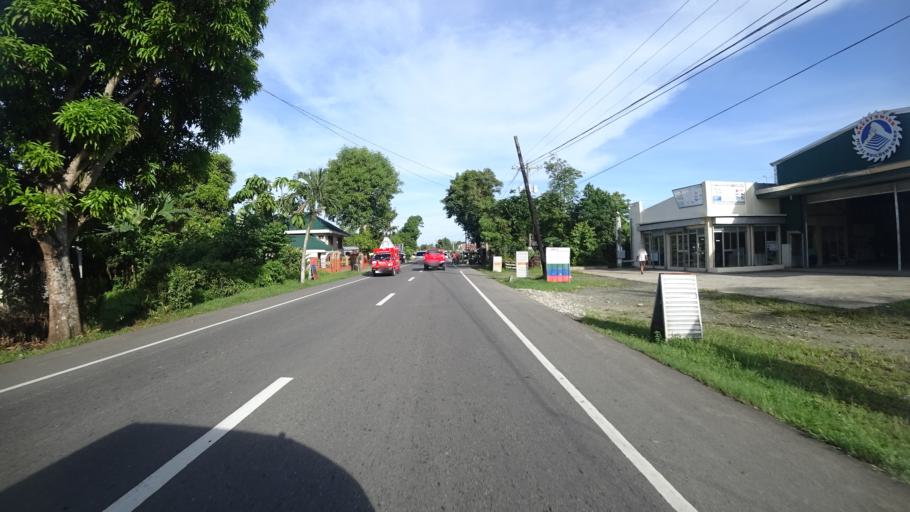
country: PH
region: Eastern Visayas
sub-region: Province of Leyte
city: Santa Fe
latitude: 11.1915
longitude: 124.8944
